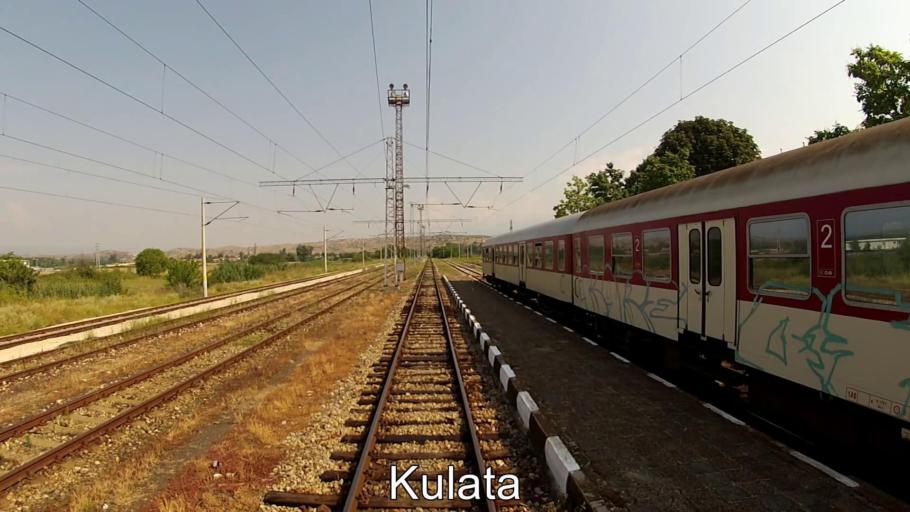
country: GR
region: Central Macedonia
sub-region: Nomos Serron
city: Charopo
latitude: 41.3933
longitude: 23.3613
